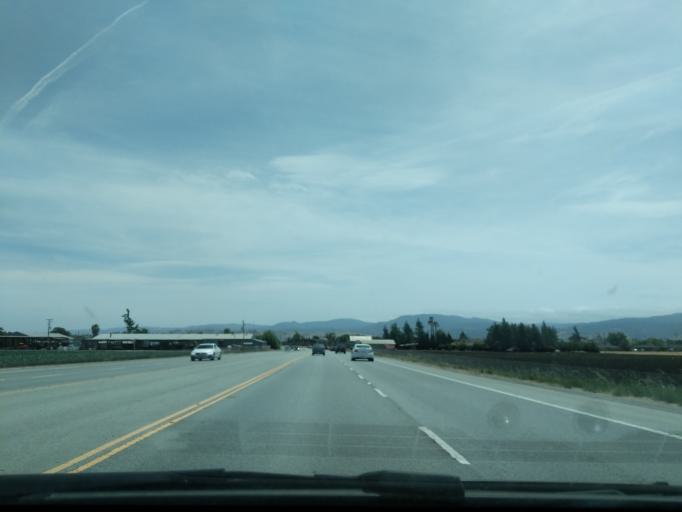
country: US
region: California
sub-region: San Benito County
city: Hollister
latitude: 36.8596
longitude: -121.3908
